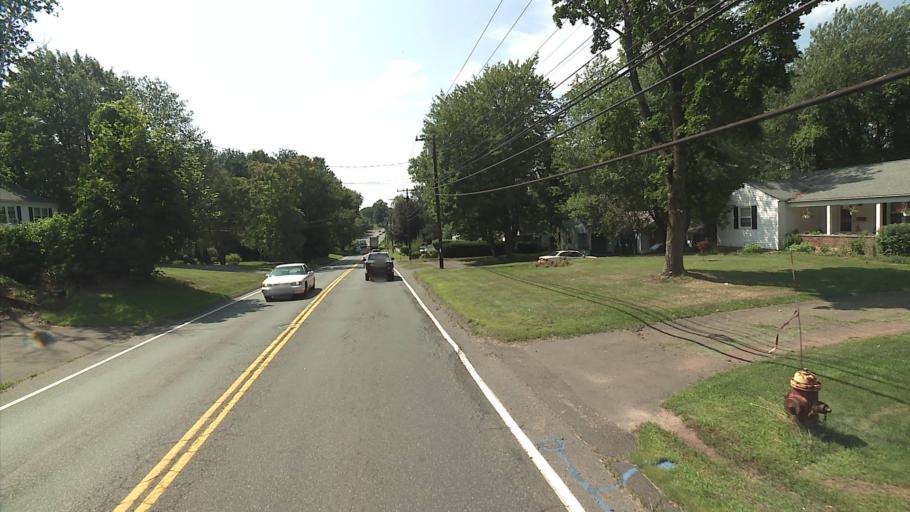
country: US
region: Connecticut
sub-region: Hartford County
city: Windsor
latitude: 41.8553
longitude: -72.6745
